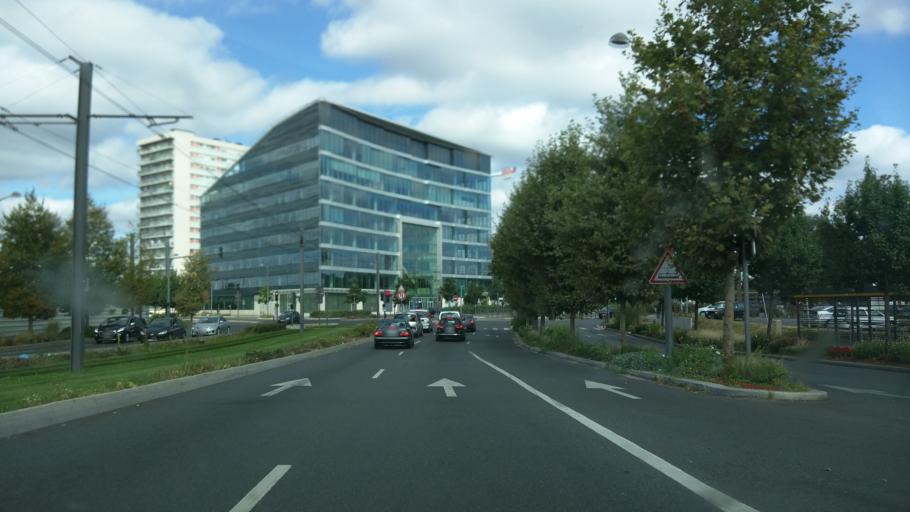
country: FR
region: Ile-de-France
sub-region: Departement du Val-d'Oise
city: Bezons
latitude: 48.9221
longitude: 2.2185
